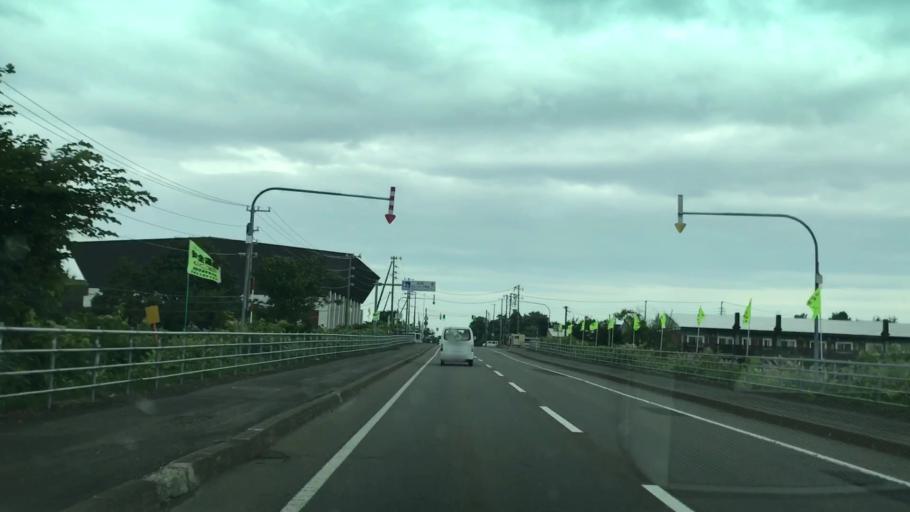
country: JP
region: Hokkaido
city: Iwanai
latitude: 42.7873
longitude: 140.2344
